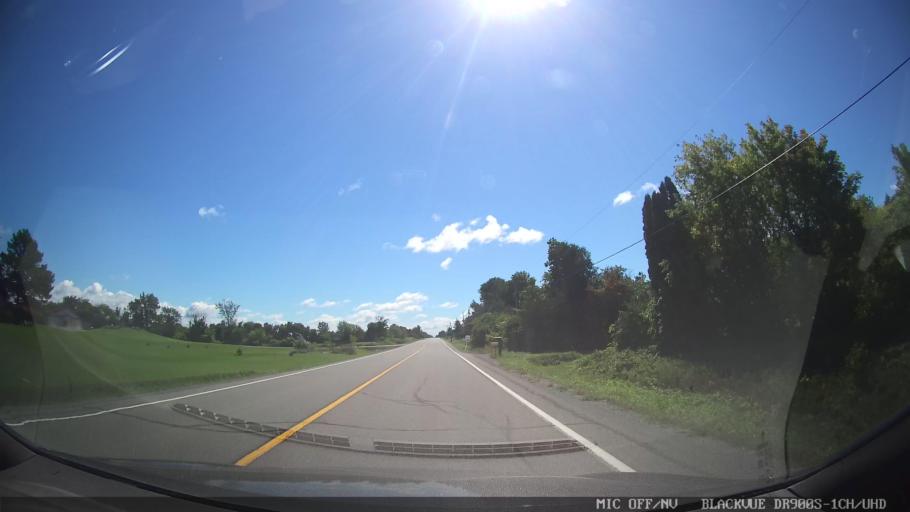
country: CA
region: Ontario
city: Bells Corners
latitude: 45.1787
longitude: -75.7752
